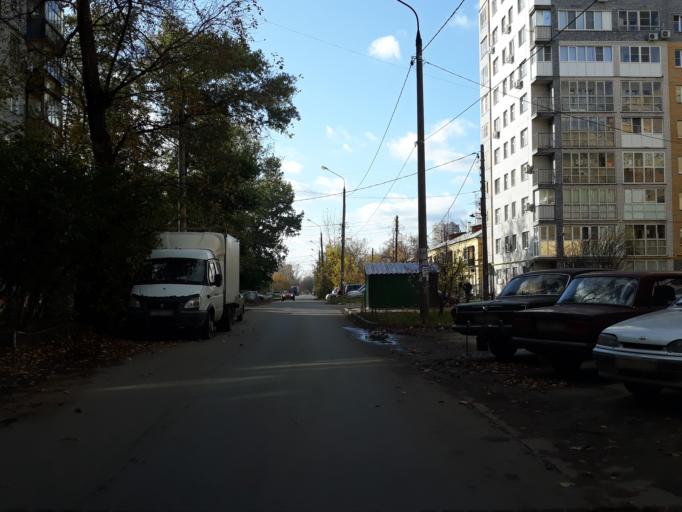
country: RU
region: Nizjnij Novgorod
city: Nizhniy Novgorod
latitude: 56.3033
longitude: 43.9372
